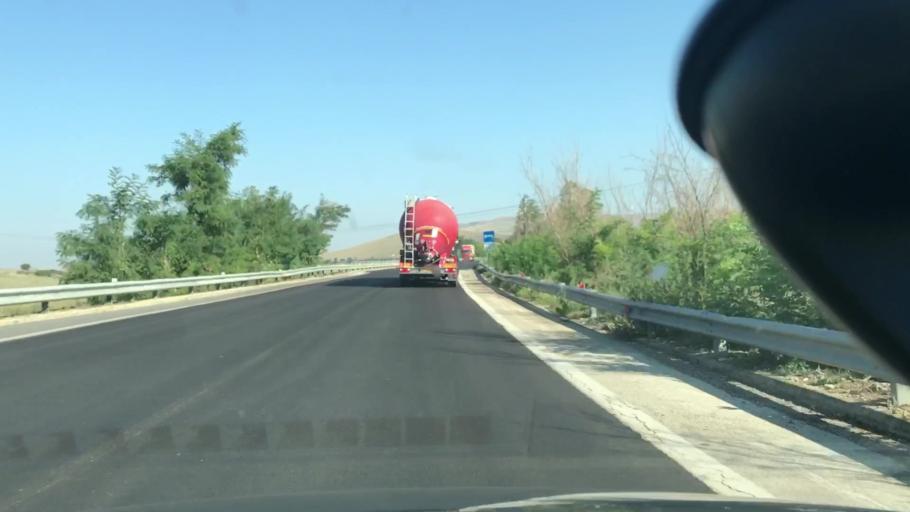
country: IT
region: Basilicate
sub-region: Provincia di Matera
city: Irsina
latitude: 40.7971
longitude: 16.2753
